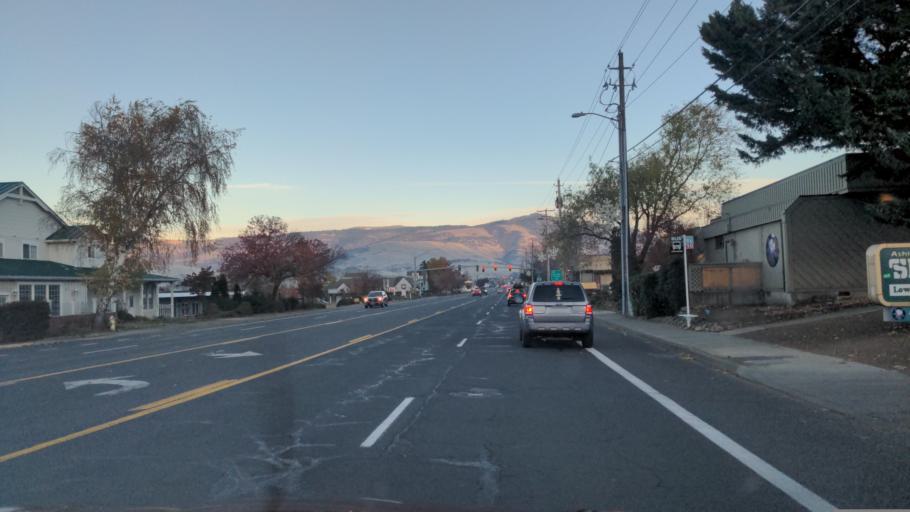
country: US
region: Oregon
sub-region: Jackson County
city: Ashland
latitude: 42.1853
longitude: -122.6736
